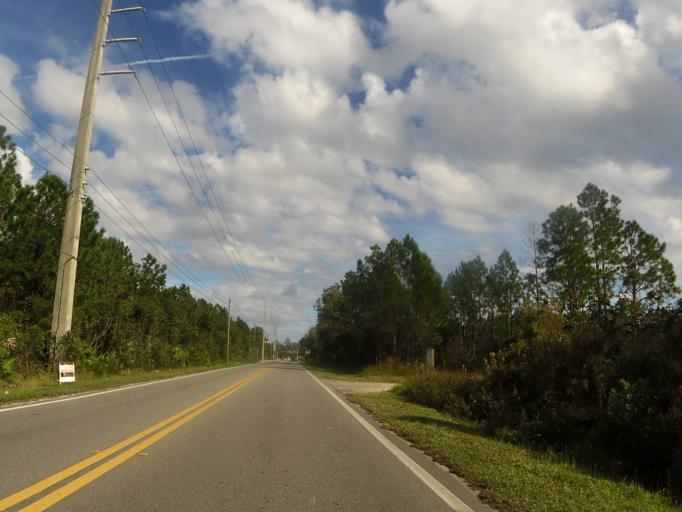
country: US
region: Florida
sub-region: Saint Johns County
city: Villano Beach
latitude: 30.0113
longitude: -81.3968
